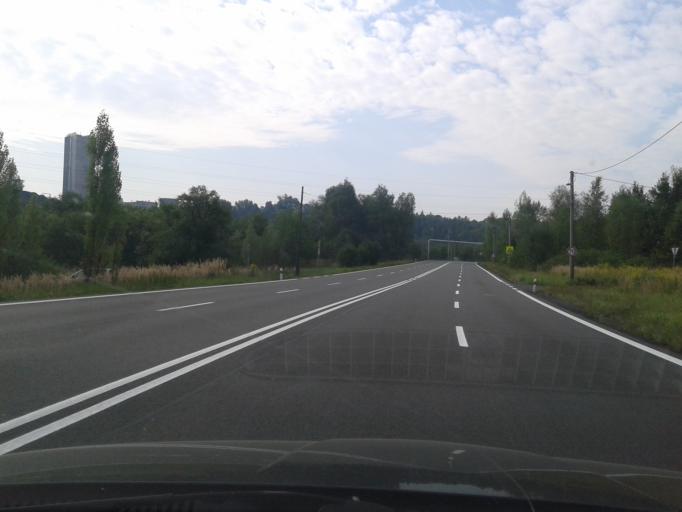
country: CZ
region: Moravskoslezsky
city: Orlova
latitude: 49.8352
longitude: 18.4366
